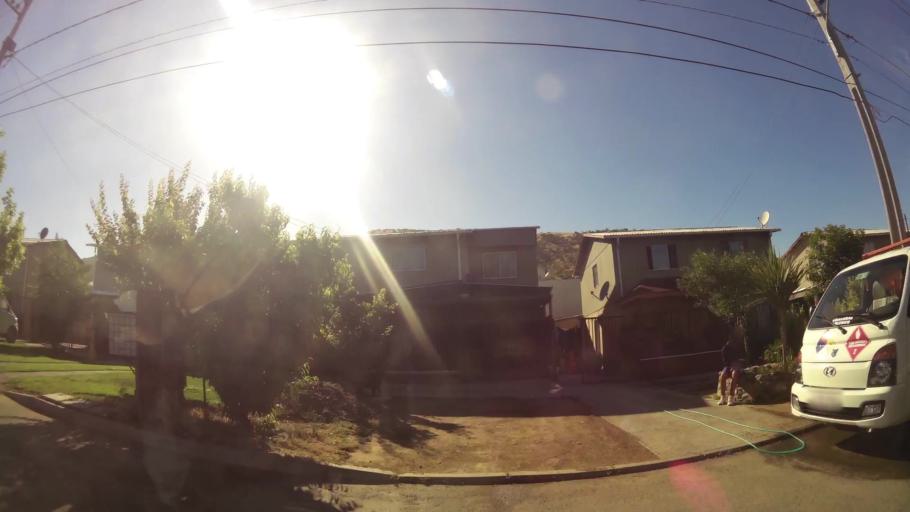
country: CL
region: Santiago Metropolitan
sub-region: Provincia de Chacabuco
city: Lampa
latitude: -33.3933
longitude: -71.1209
